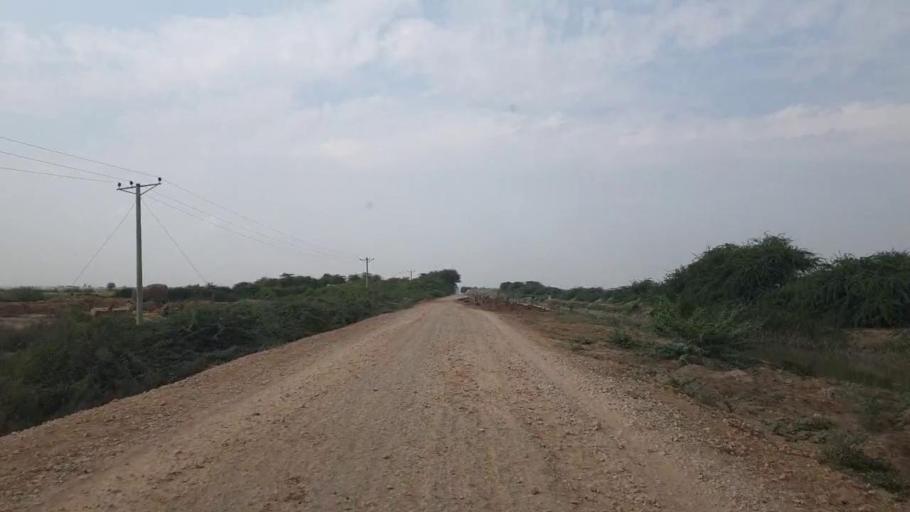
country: PK
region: Sindh
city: Kario
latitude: 24.6209
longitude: 68.5819
